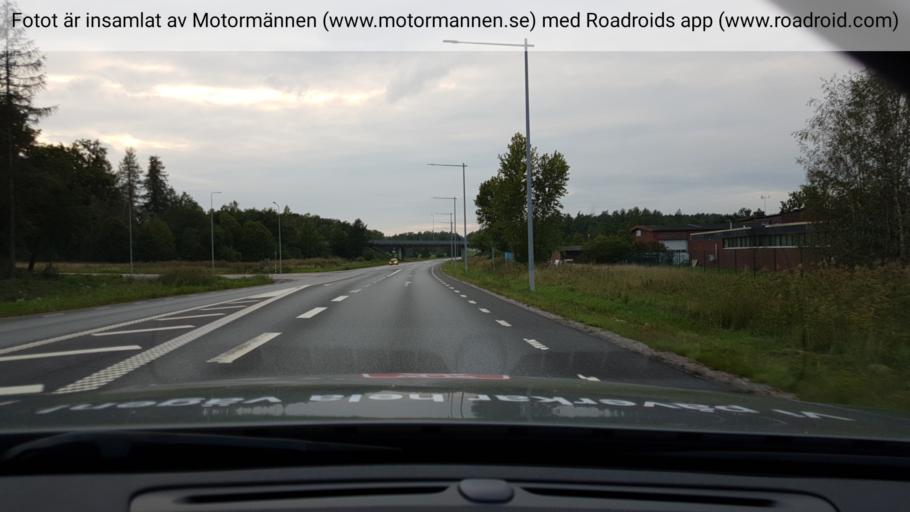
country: SE
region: Vaestmanland
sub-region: Arboga Kommun
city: Arboga
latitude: 59.3890
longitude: 15.8402
